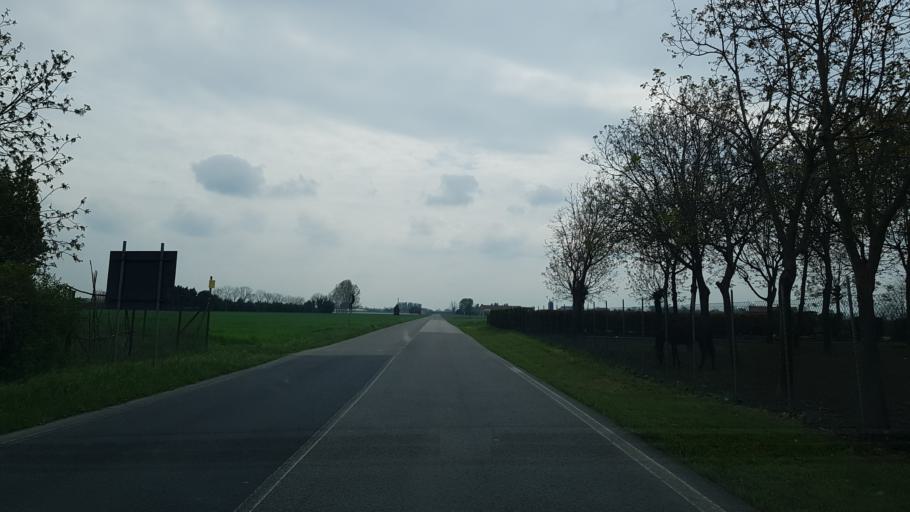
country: IT
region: Veneto
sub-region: Provincia di Verona
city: Albaredo d'Adige
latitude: 45.2975
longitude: 11.2768
